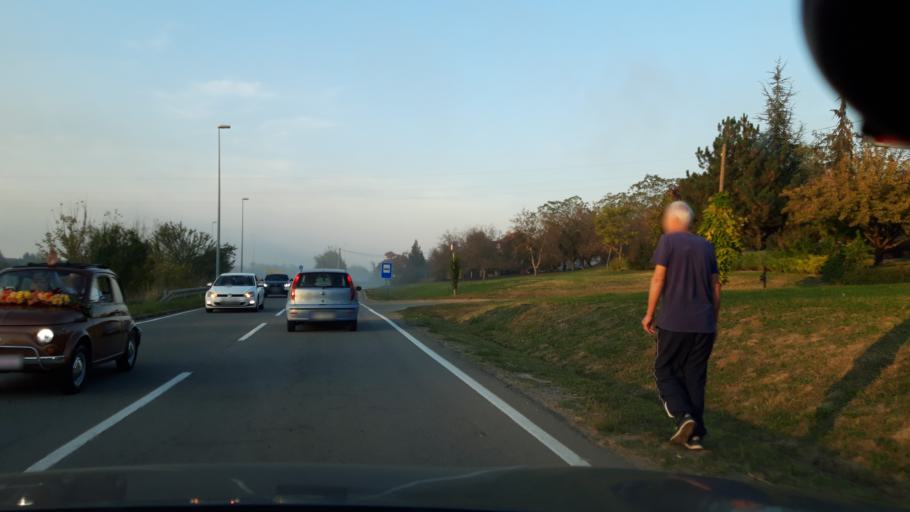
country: RS
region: Autonomna Pokrajina Vojvodina
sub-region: Juznobacki Okrug
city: Novi Sad
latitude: 45.2093
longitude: 19.8409
